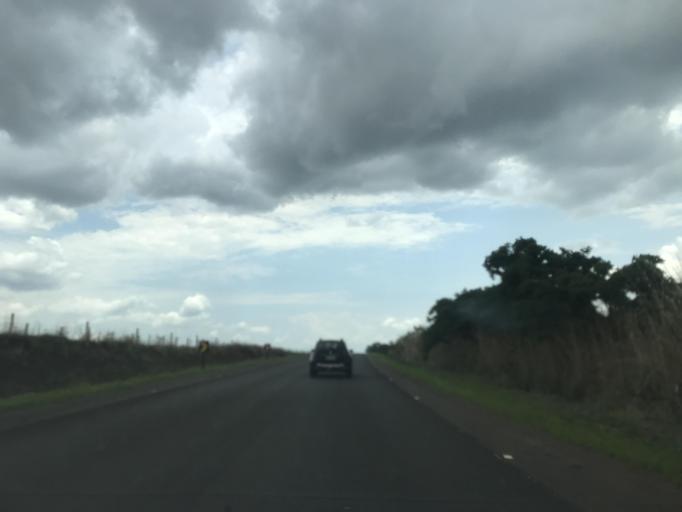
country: BR
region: Goias
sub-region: Vianopolis
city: Vianopolis
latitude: -16.9056
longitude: -48.5521
